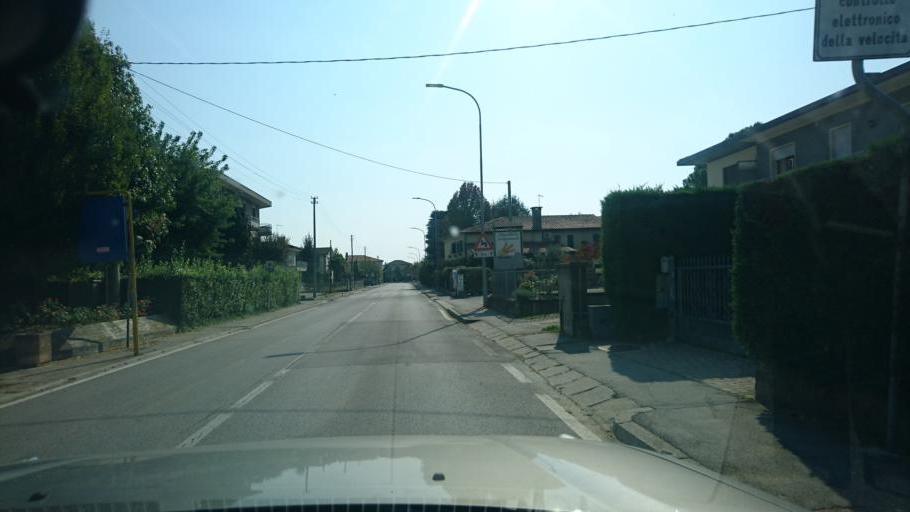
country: IT
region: Veneto
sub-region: Provincia di Padova
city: Campodoro
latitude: 45.5100
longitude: 11.7414
